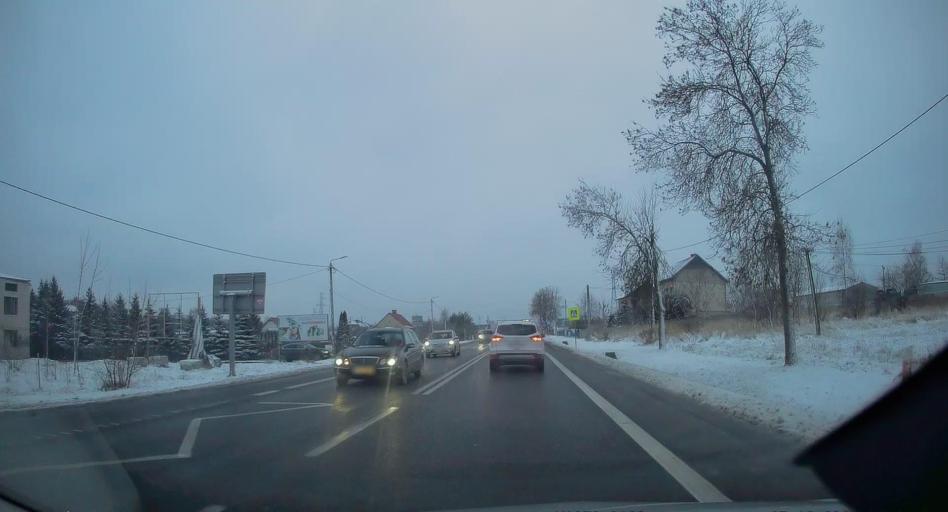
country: PL
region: Swietokrzyskie
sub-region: Powiat kielecki
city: Kostomloty Drugie
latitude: 50.9134
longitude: 20.5750
